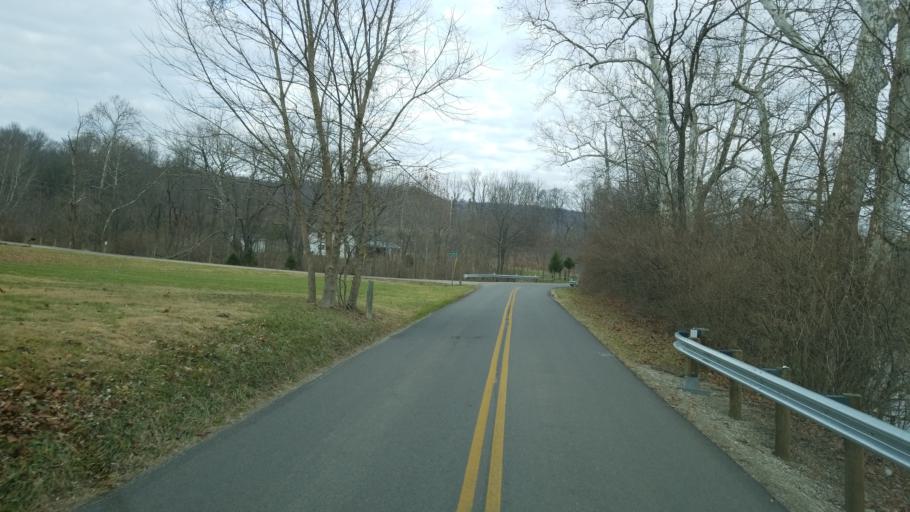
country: US
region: Ohio
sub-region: Highland County
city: Greenfield
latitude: 39.2362
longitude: -83.2874
